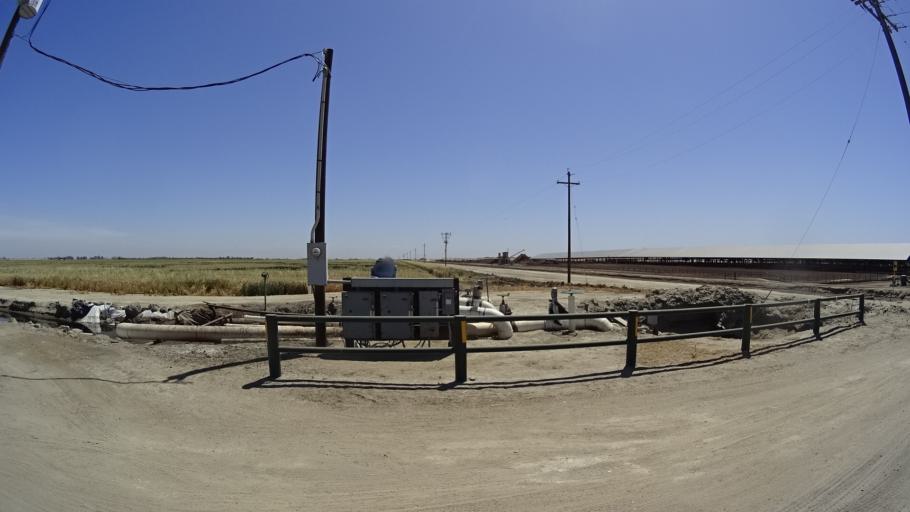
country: US
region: California
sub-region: Kings County
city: Home Garden
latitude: 36.1894
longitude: -119.6906
